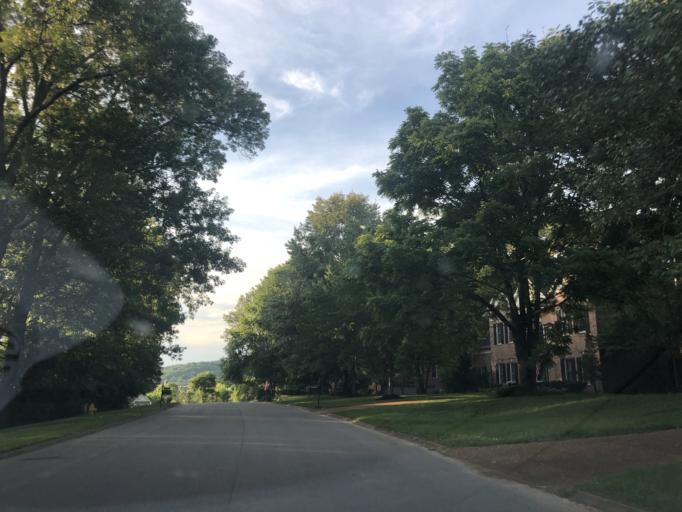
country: US
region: Tennessee
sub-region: Davidson County
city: Forest Hills
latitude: 36.0487
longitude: -86.9182
